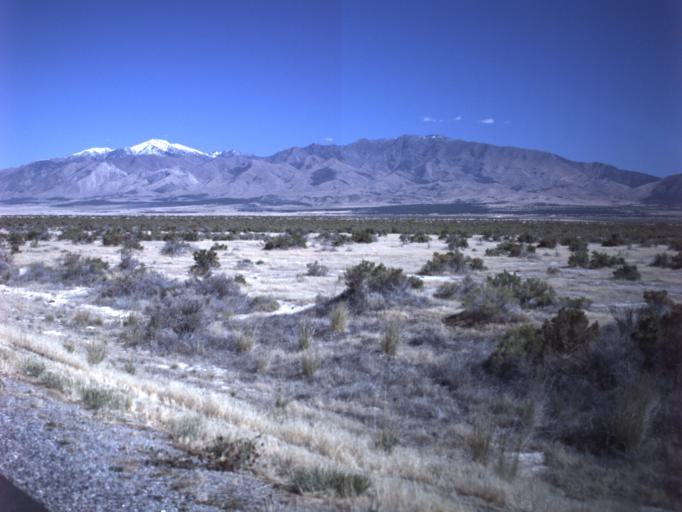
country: US
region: Utah
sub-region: Tooele County
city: Grantsville
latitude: 40.2621
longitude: -112.7408
